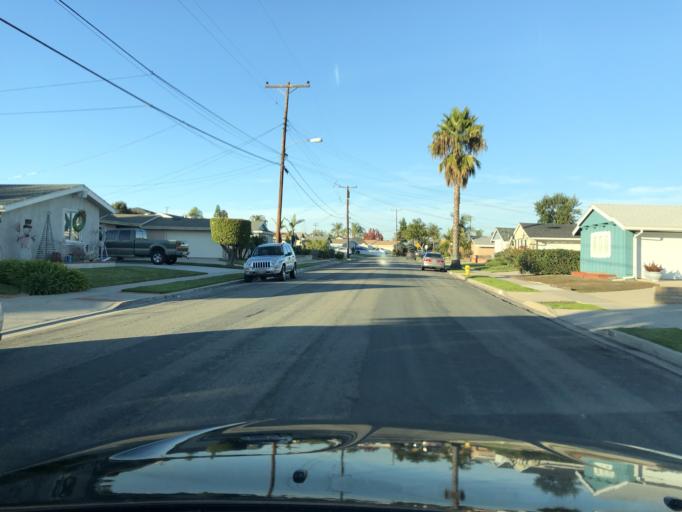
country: US
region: California
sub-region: San Diego County
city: La Jolla
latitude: 32.8198
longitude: -117.1949
